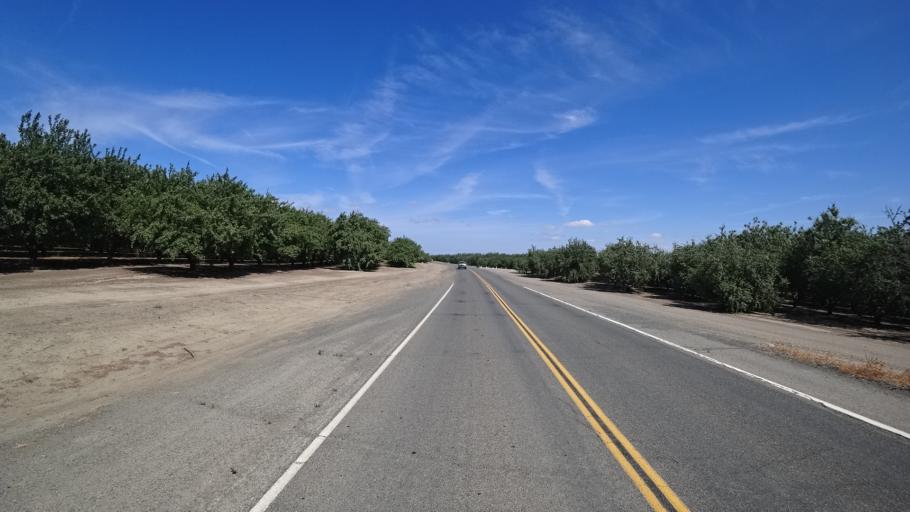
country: US
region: California
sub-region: Kings County
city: Kettleman City
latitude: 35.9624
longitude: -119.9367
